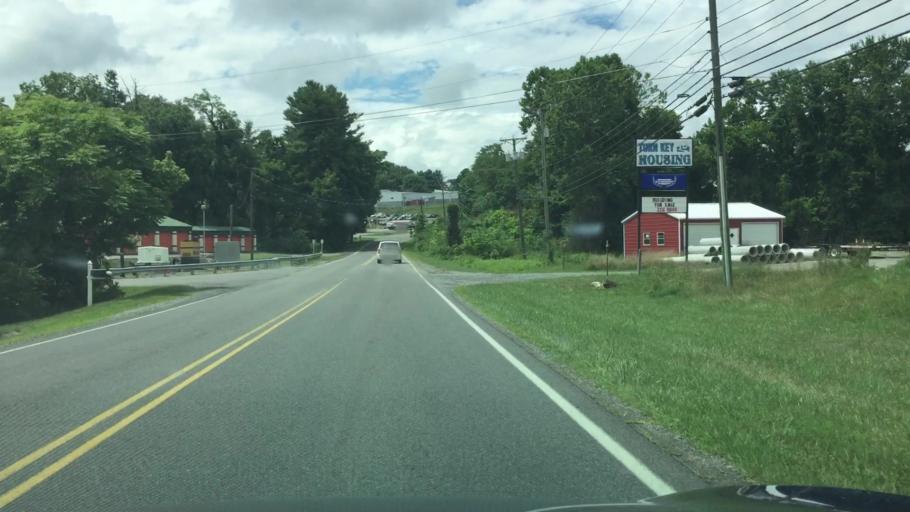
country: US
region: Virginia
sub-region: Wythe County
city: Wytheville
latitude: 36.9471
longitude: -81.0629
